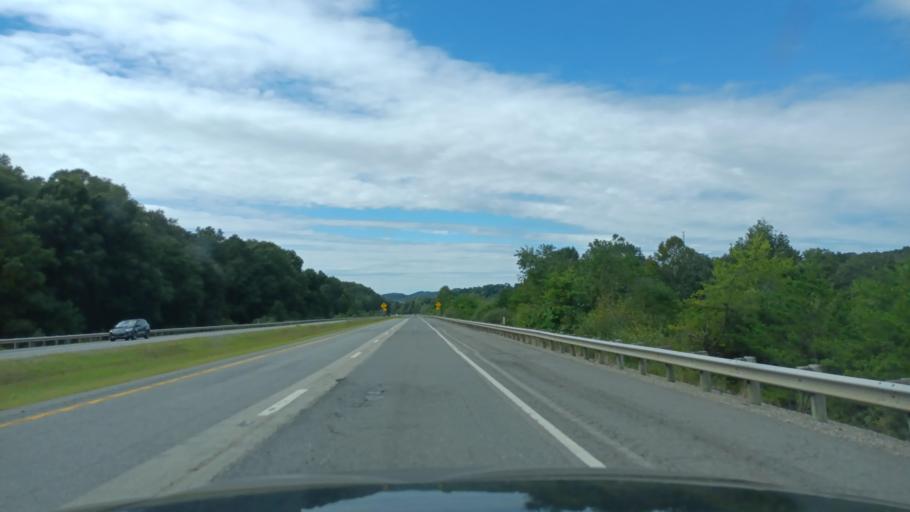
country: US
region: West Virginia
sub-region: Doddridge County
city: West Union
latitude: 39.2744
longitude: -80.8680
